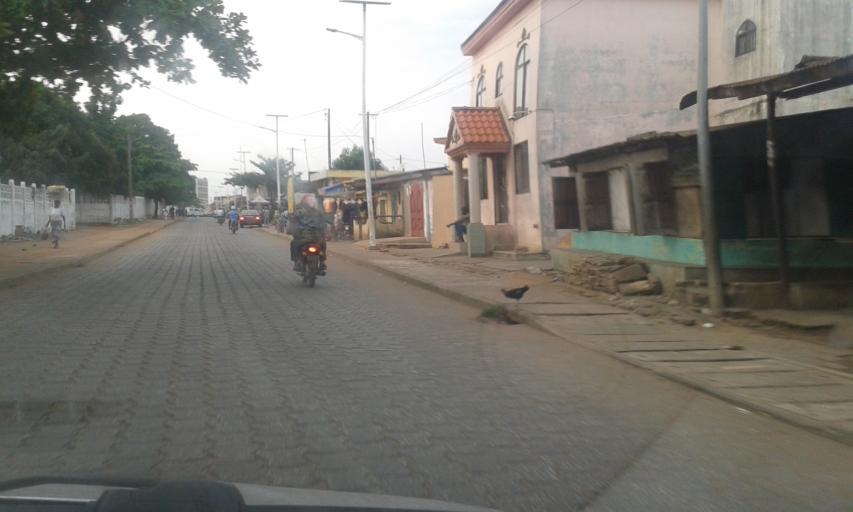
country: BJ
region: Queme
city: Porto-Novo
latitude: 6.4803
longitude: 2.6204
